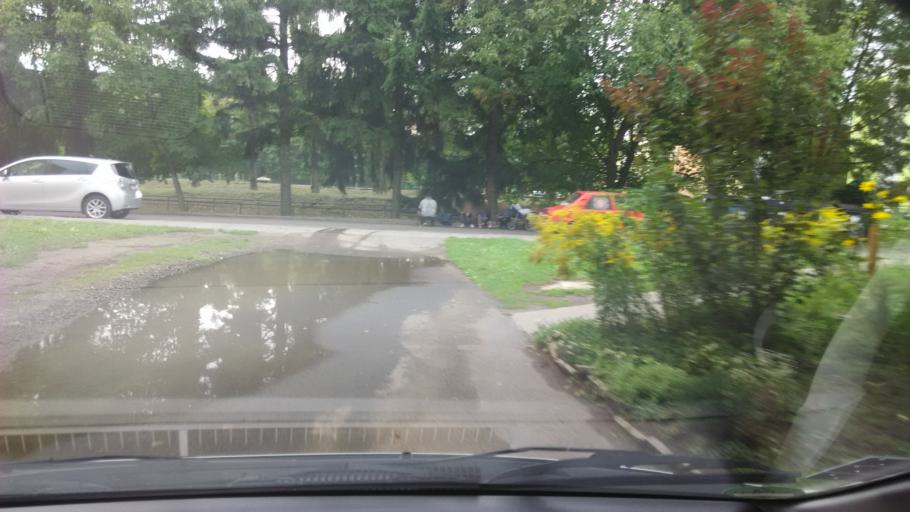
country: SK
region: Nitriansky
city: Levice
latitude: 48.2125
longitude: 18.6010
